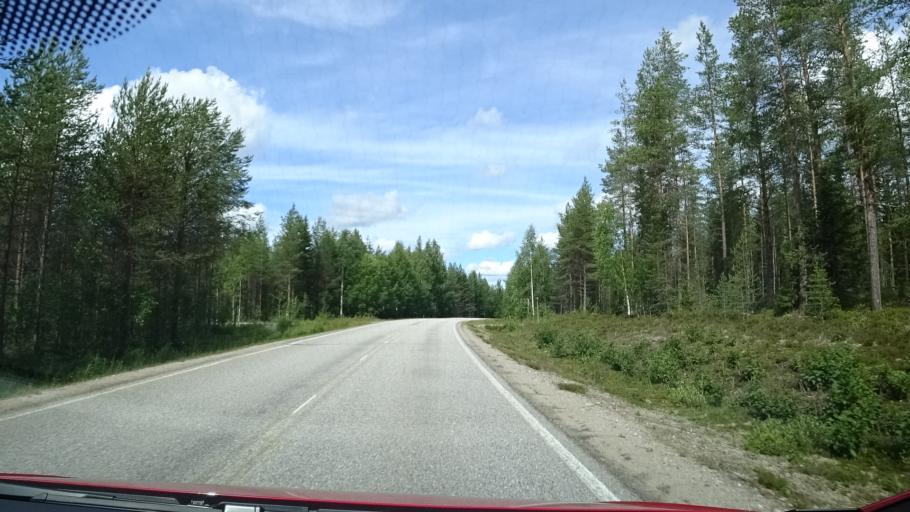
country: FI
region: Kainuu
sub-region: Kehys-Kainuu
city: Kuhmo
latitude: 64.4478
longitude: 29.7886
